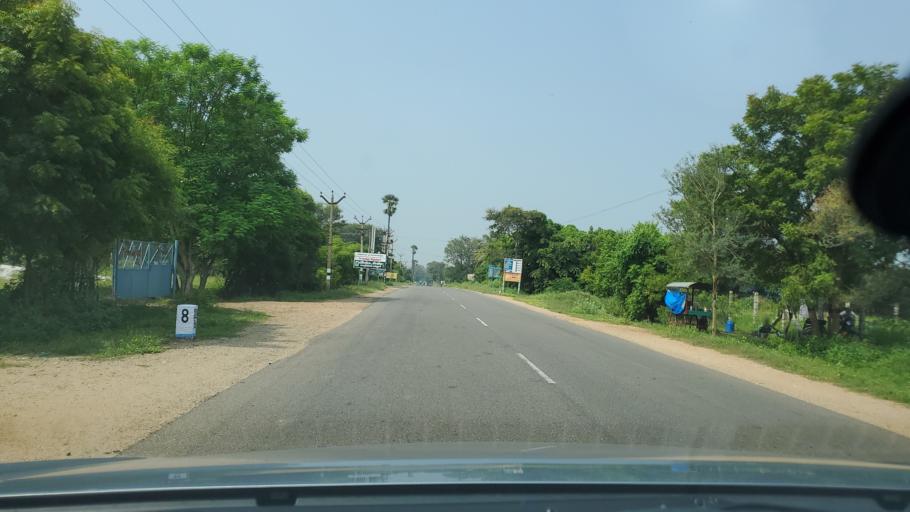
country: IN
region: Tamil Nadu
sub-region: Erode
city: Chennimalai
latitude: 11.1884
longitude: 77.6159
